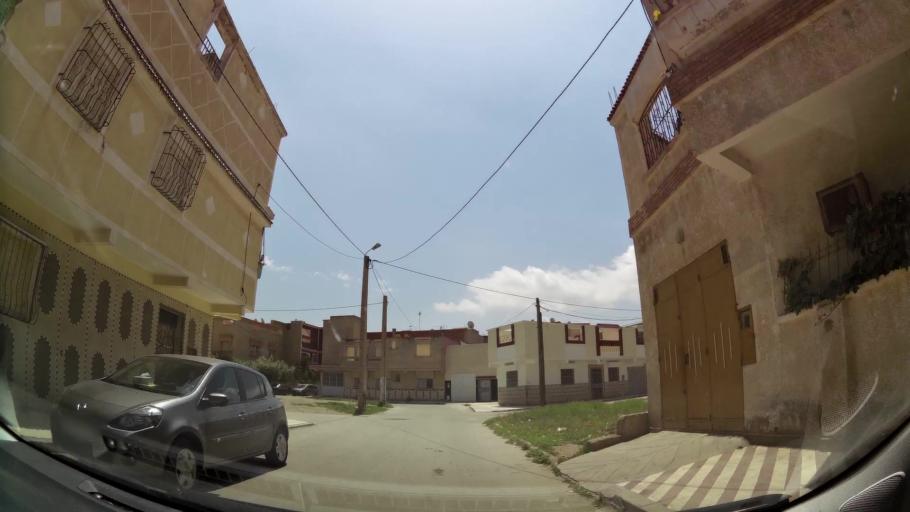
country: MA
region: Oriental
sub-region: Oujda-Angad
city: Oujda
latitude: 34.6879
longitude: -1.8922
